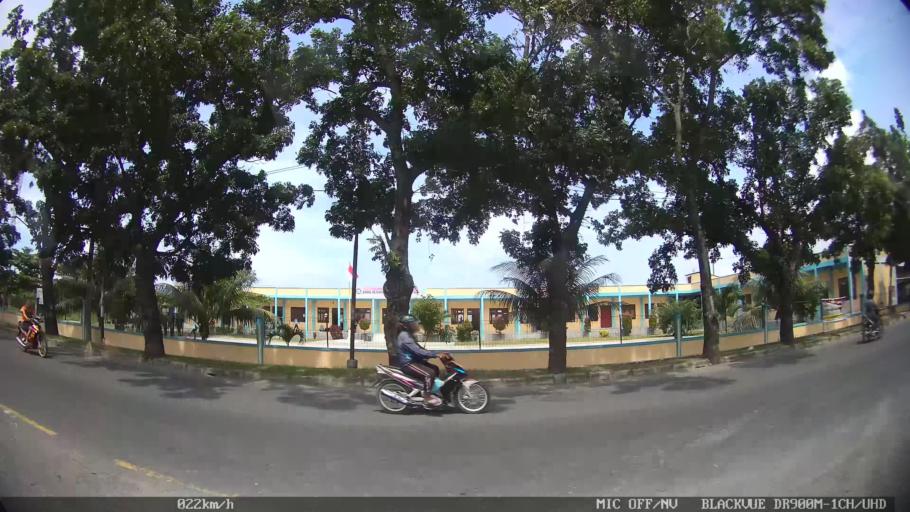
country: ID
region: North Sumatra
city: Labuhan Deli
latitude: 3.6761
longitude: 98.6658
